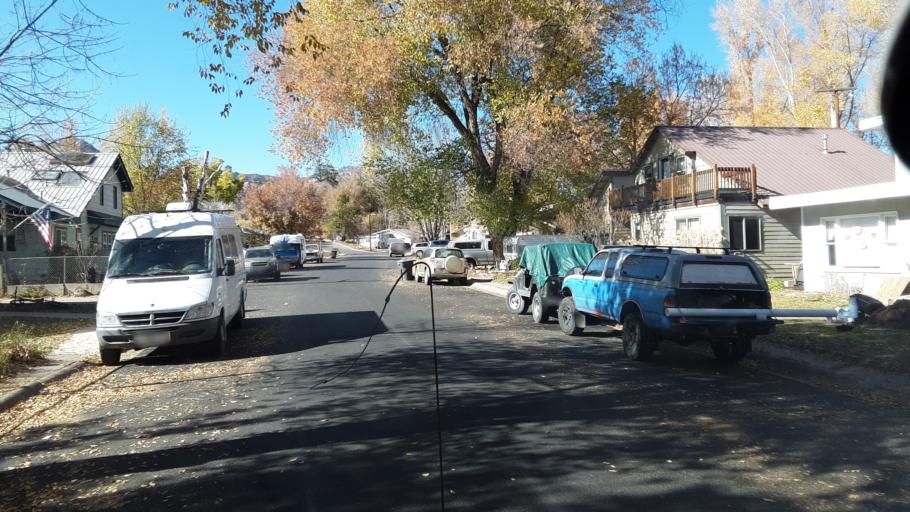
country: US
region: Colorado
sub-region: La Plata County
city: Durango
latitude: 37.2853
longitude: -107.8732
